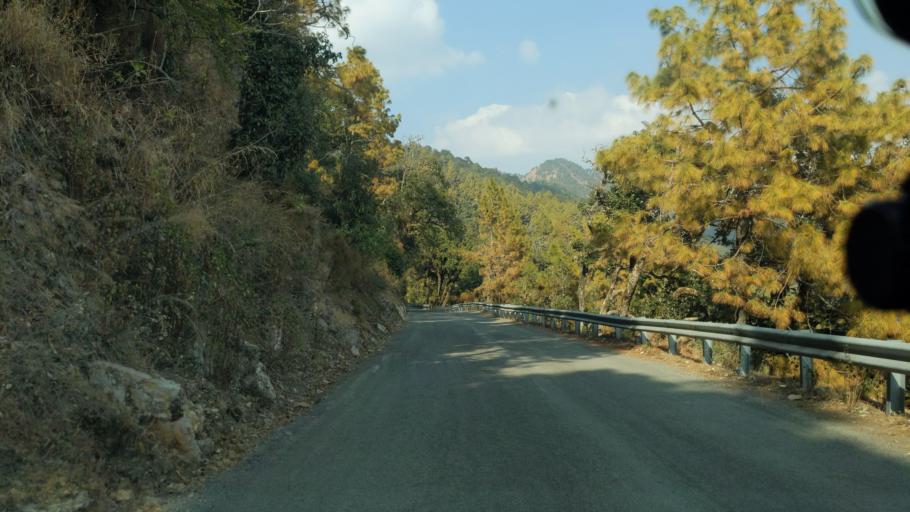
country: IN
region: Uttarakhand
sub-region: Naini Tal
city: Bhowali
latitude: 29.3990
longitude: 79.5352
